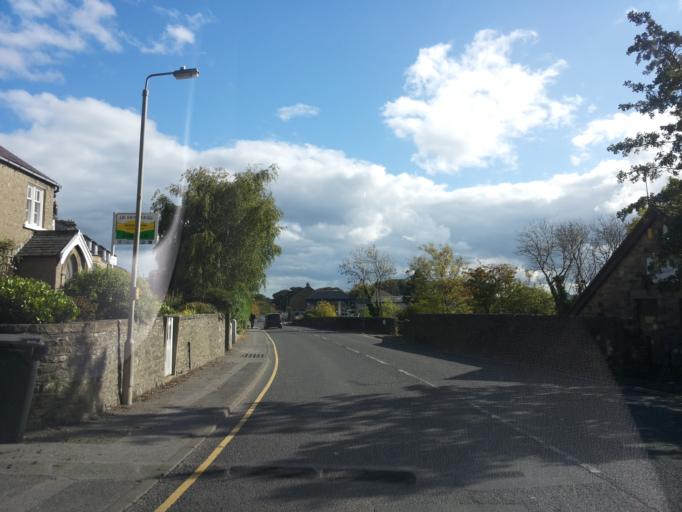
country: GB
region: England
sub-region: North Yorkshire
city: Leyburn
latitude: 54.3086
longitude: -1.8263
